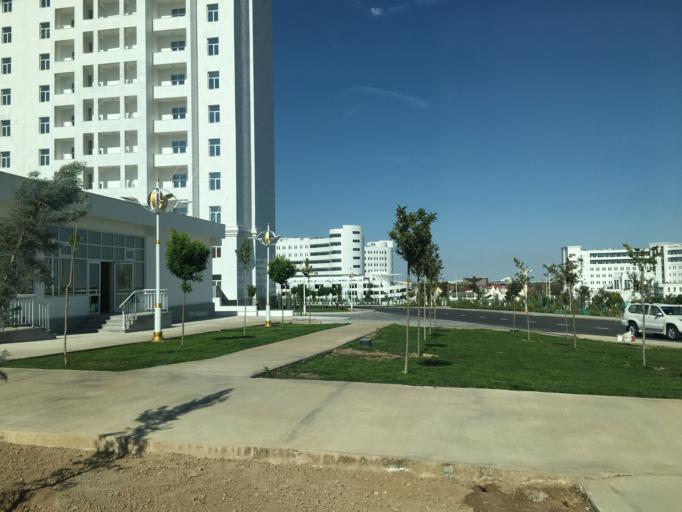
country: TM
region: Ahal
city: Ashgabat
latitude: 37.9381
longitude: 58.3619
